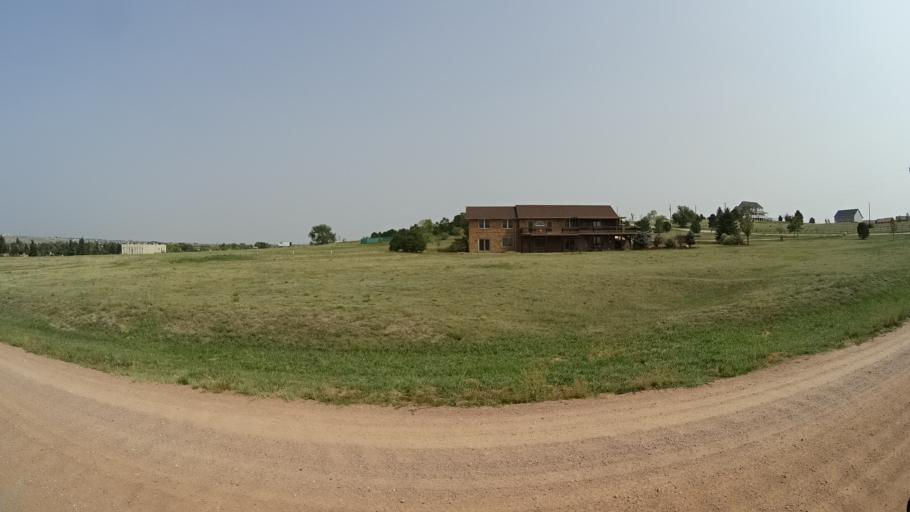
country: US
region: Colorado
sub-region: El Paso County
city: Cimarron Hills
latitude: 38.9151
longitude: -104.7291
